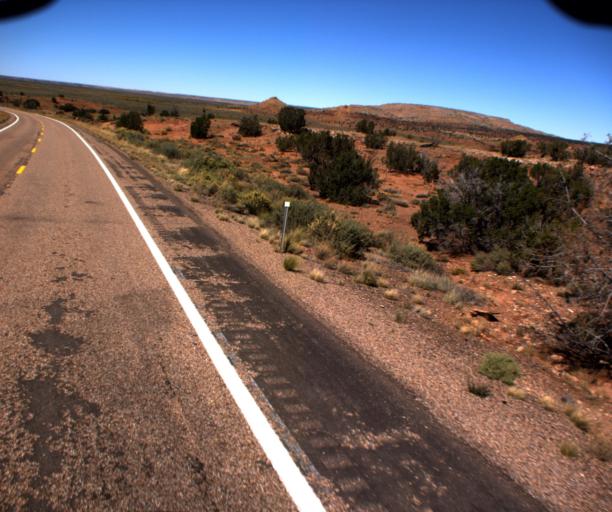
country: US
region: Arizona
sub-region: Apache County
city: Saint Johns
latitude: 34.5847
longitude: -109.5406
